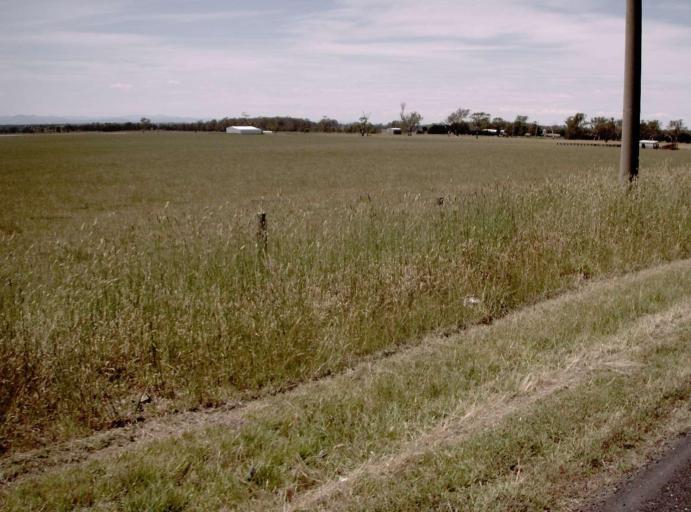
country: AU
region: Victoria
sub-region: Latrobe
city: Traralgon
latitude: -38.1753
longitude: 146.6501
